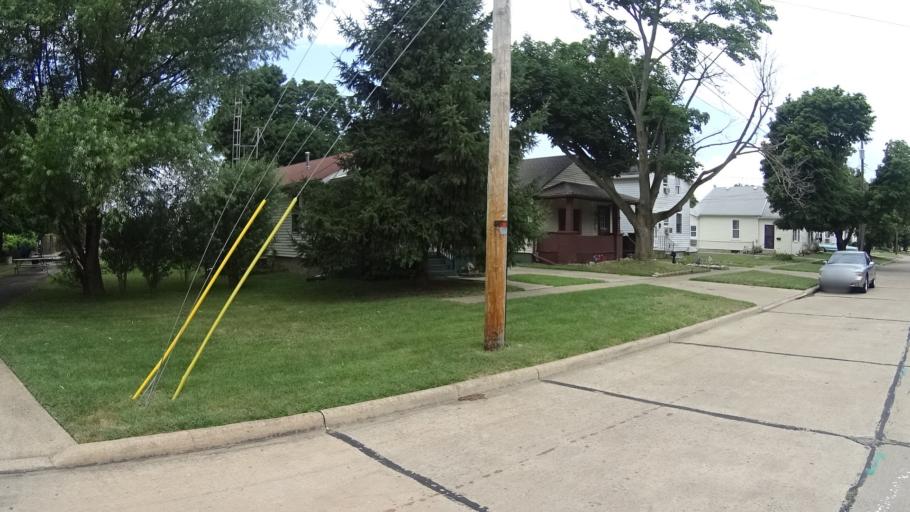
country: US
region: Ohio
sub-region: Erie County
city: Sandusky
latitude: 41.4413
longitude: -82.7244
